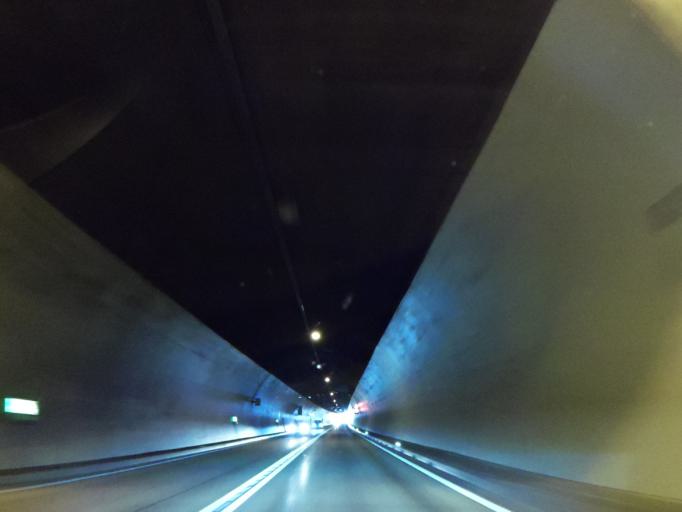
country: AT
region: Tyrol
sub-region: Politischer Bezirk Reutte
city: Vils
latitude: 47.5626
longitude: 10.6567
